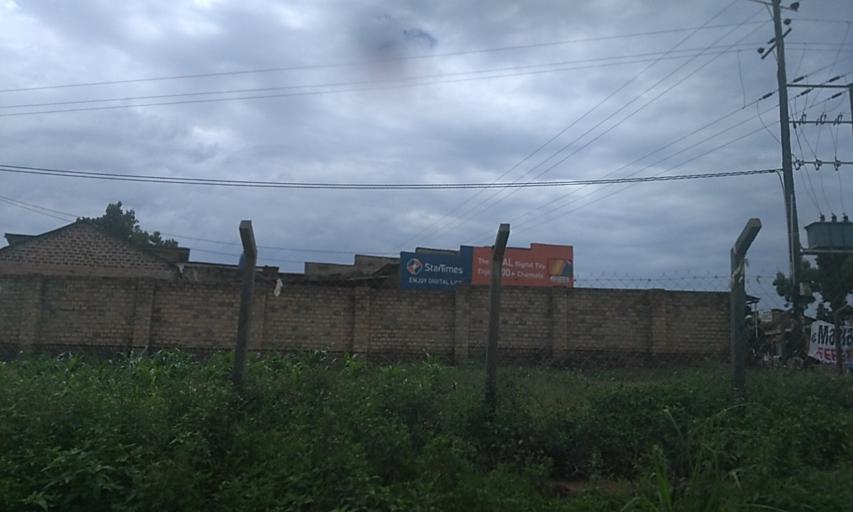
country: UG
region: Central Region
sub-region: Wakiso District
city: Bweyogerere
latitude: 0.3949
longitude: 32.6867
